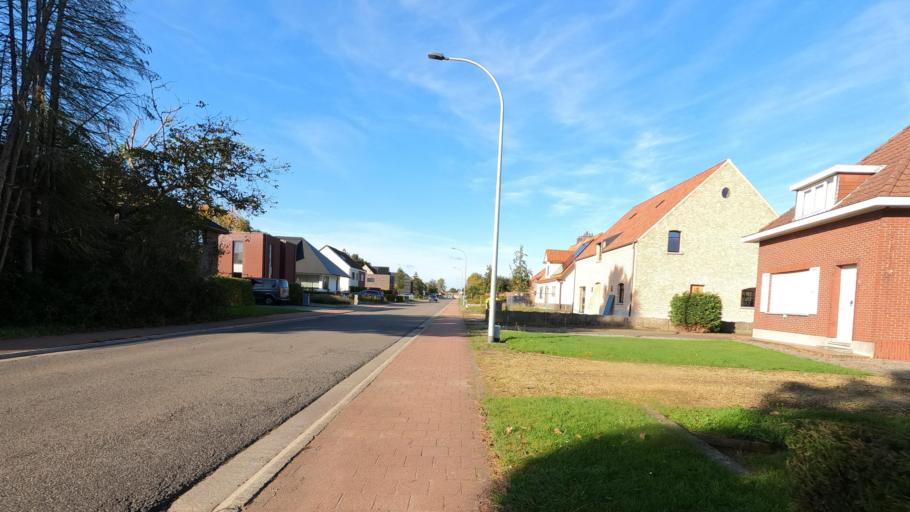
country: BE
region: Flanders
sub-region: Provincie Antwerpen
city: Heist-op-den-Berg
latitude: 51.0534
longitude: 4.7500
